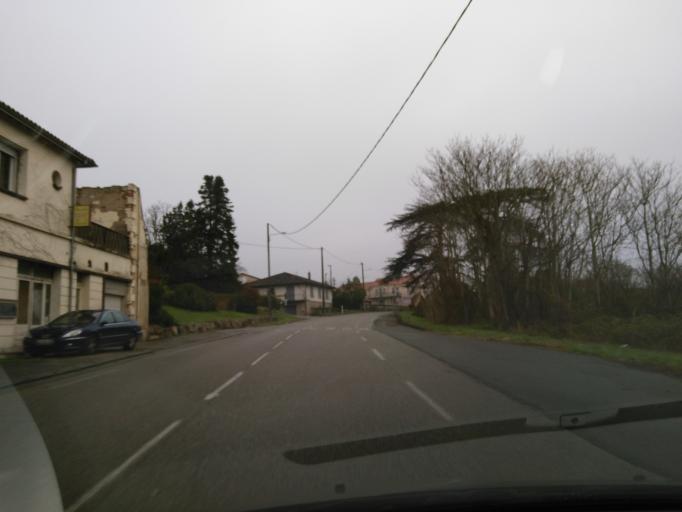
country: FR
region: Aquitaine
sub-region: Departement du Lot-et-Garonne
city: Cancon
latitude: 44.4959
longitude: 0.6683
